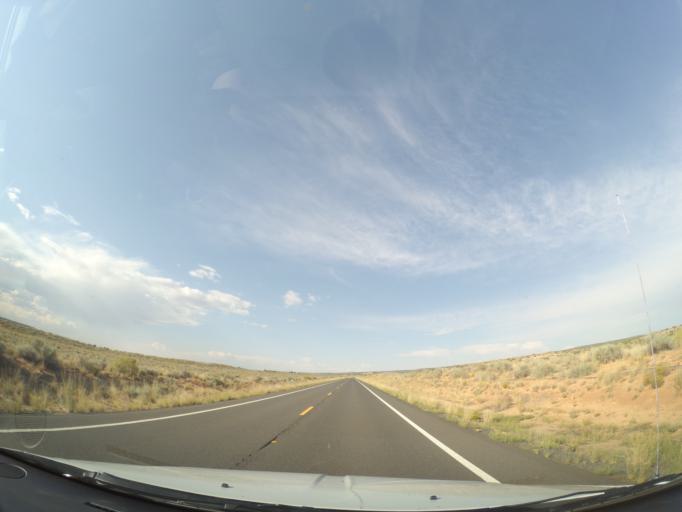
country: US
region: Arizona
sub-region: Coconino County
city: Kaibito
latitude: 36.4848
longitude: -111.4133
